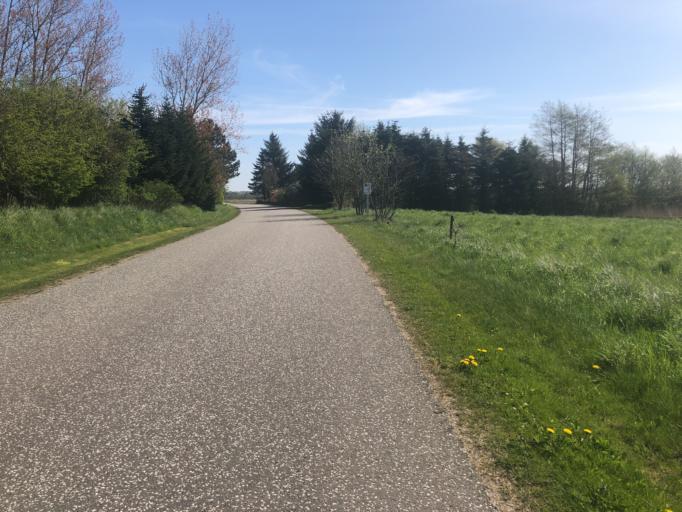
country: DK
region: Central Jutland
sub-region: Holstebro Kommune
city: Vinderup
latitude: 56.5719
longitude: 8.7888
